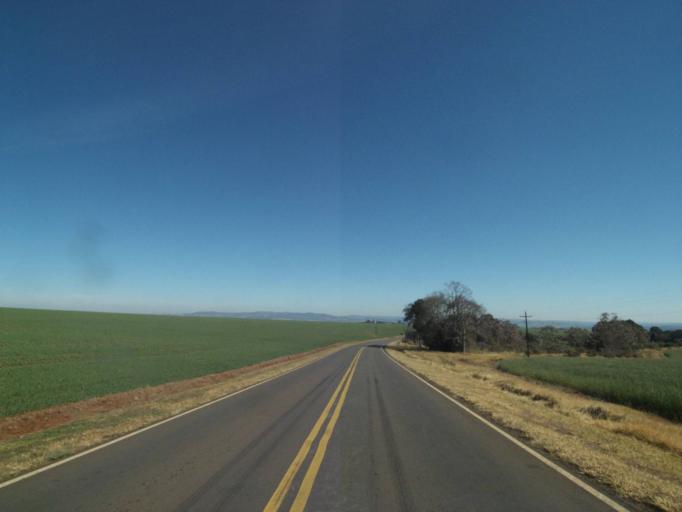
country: BR
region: Parana
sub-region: Tibagi
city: Tibagi
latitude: -24.5201
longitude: -50.3392
